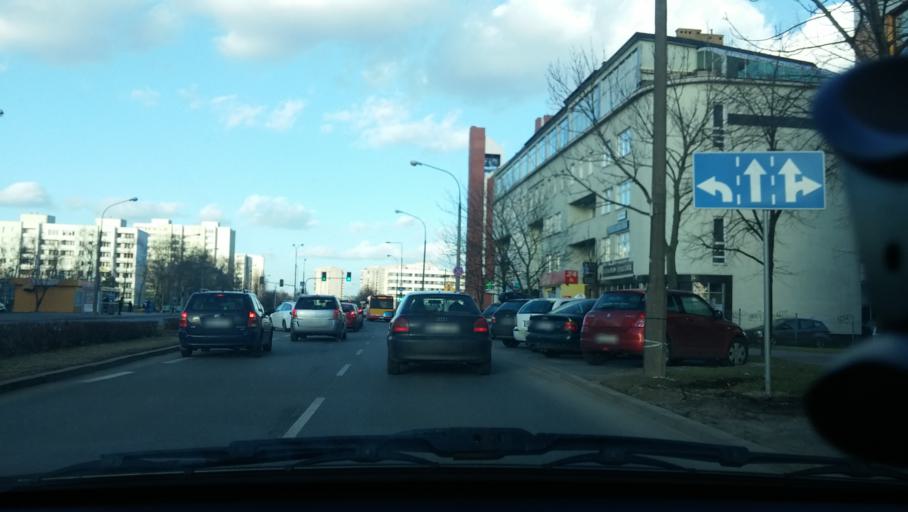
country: PL
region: Masovian Voivodeship
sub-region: Warszawa
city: Ursynow
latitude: 52.1469
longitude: 21.0409
